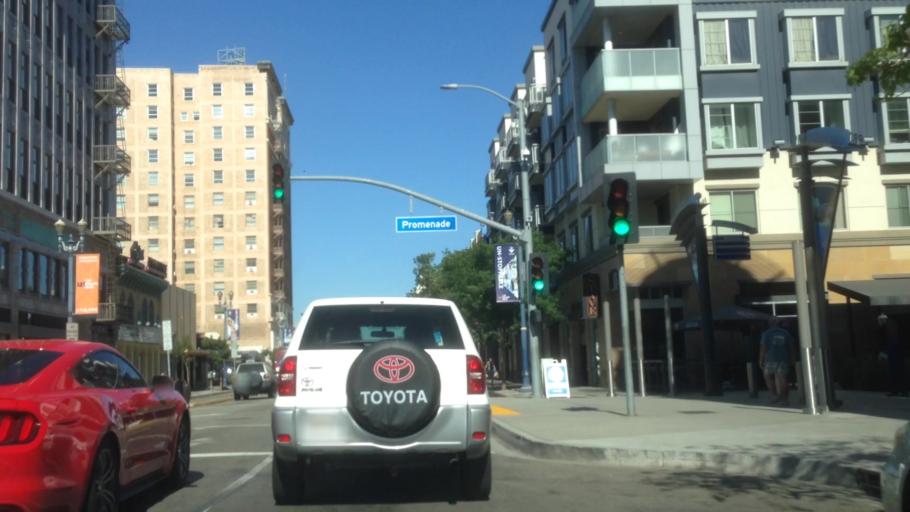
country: US
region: California
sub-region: Los Angeles County
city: Long Beach
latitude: 33.7693
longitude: -118.1913
